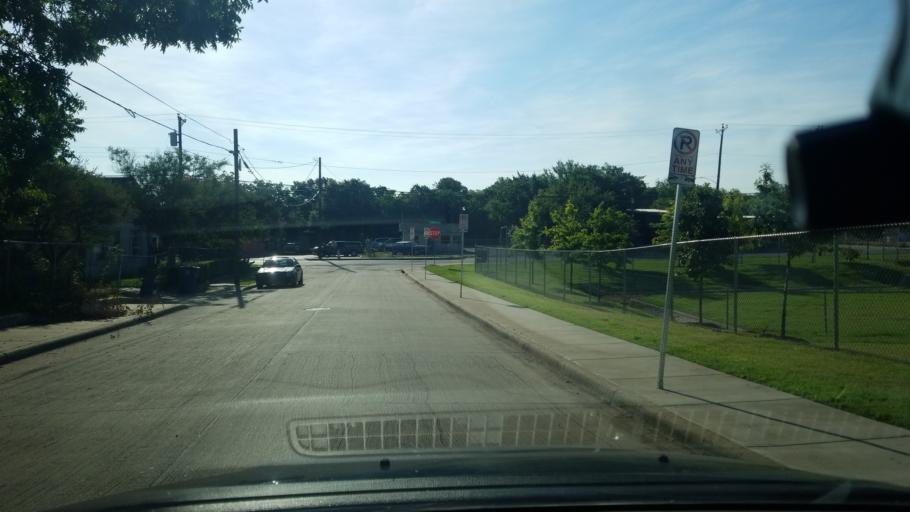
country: US
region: Texas
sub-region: Dallas County
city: Dallas
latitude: 32.7286
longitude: -96.8121
